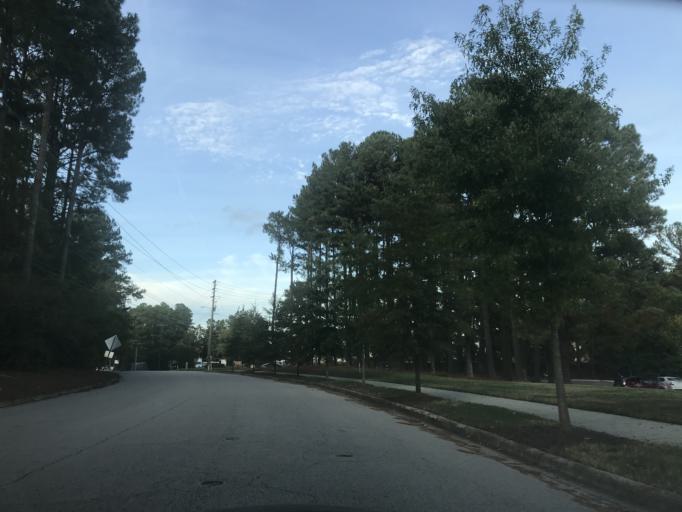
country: US
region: North Carolina
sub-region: Wake County
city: Raleigh
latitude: 35.8251
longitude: -78.6142
